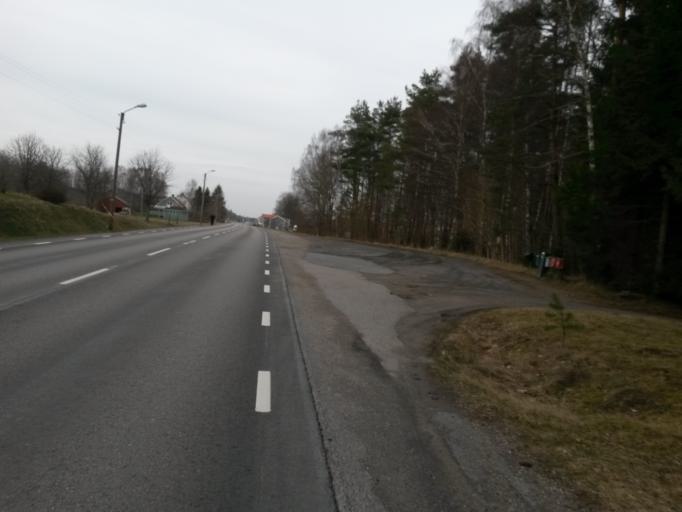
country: SE
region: Vaestra Goetaland
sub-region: Vargarda Kommun
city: Vargarda
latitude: 58.0466
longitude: 12.8153
